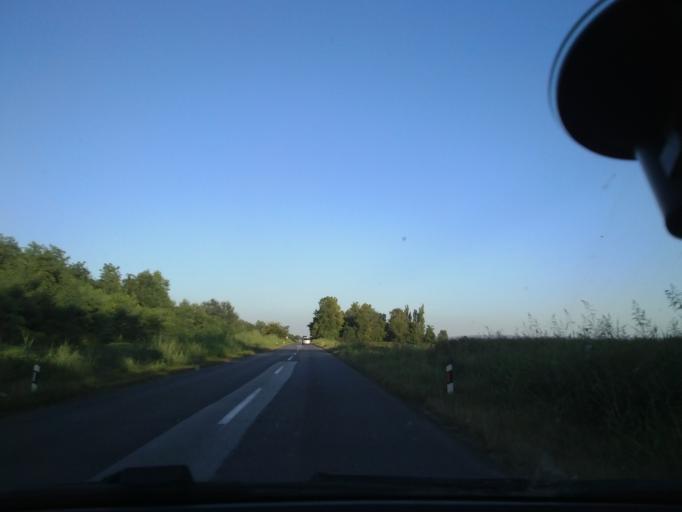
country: RS
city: Kisac
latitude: 45.3274
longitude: 19.6916
